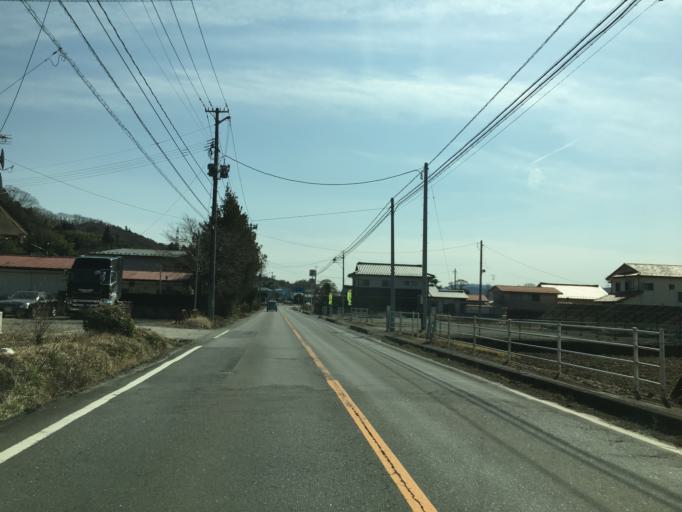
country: JP
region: Ibaraki
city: Daigo
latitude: 36.9111
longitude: 140.4174
